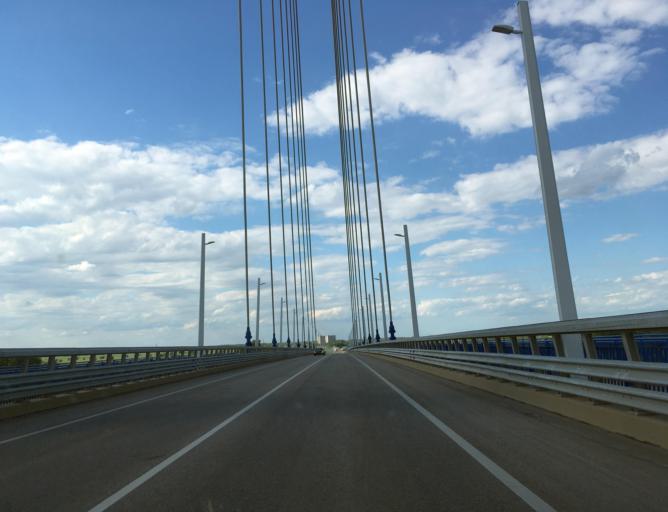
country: HU
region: Komarom-Esztergom
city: Komarom
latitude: 47.7570
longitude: 18.0846
